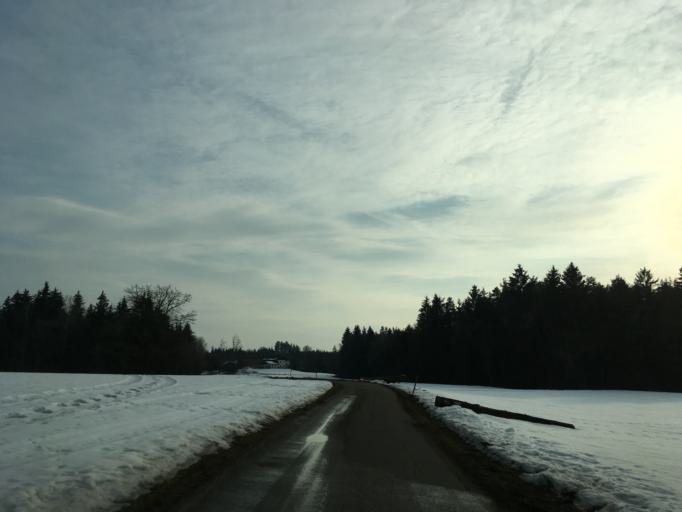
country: DE
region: Bavaria
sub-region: Upper Bavaria
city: Halfing
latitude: 47.9311
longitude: 12.2592
